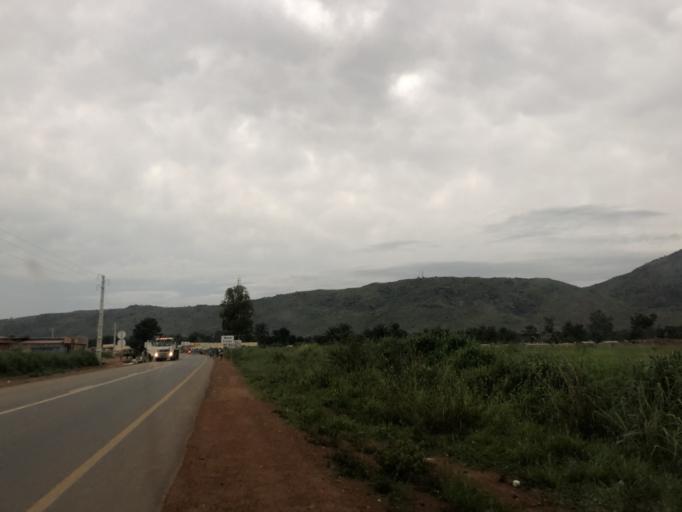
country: AO
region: Cuanza Sul
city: Uacu Cungo
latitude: -11.3459
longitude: 15.1042
